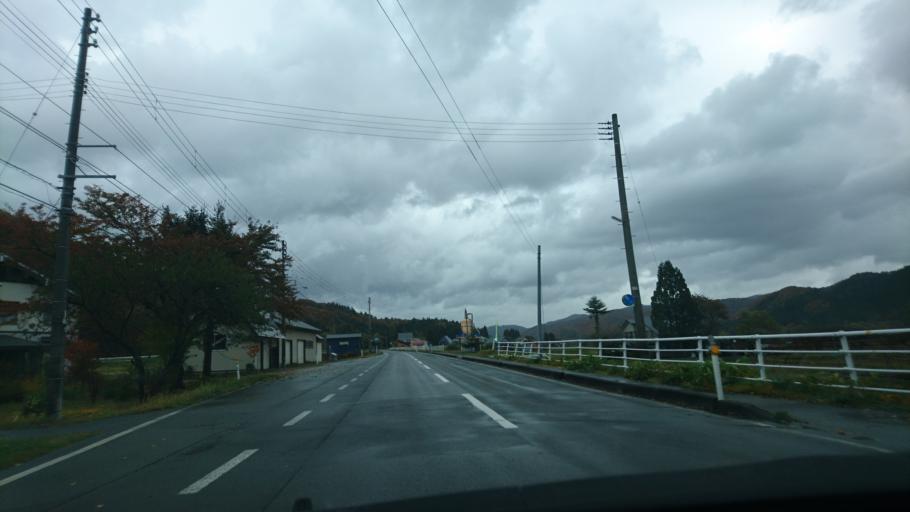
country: JP
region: Akita
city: Kakunodatemachi
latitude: 39.4847
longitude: 140.8051
